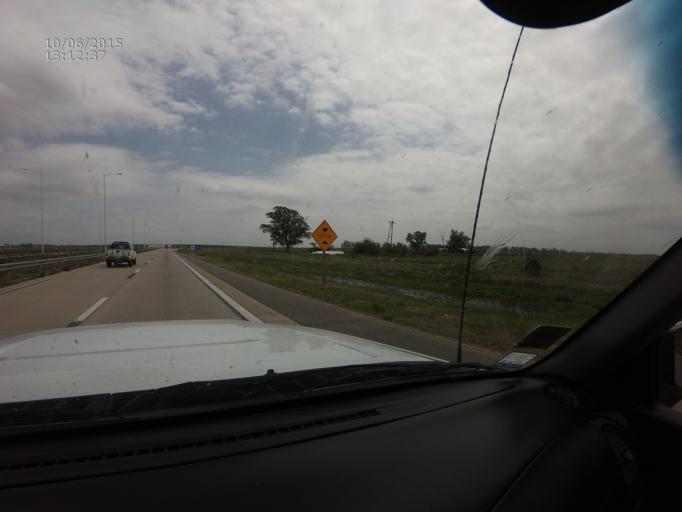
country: AR
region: Cordoba
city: General Roca
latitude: -32.7109
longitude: -61.9035
